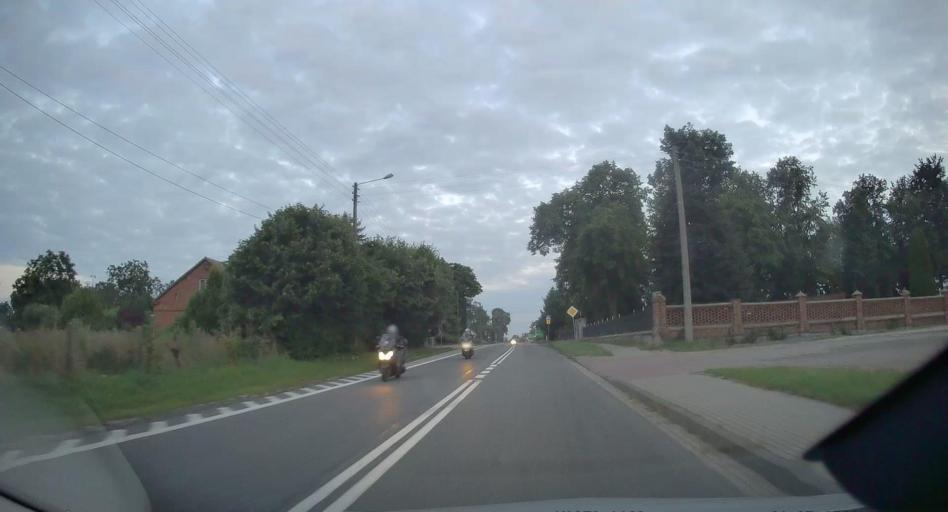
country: PL
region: Opole Voivodeship
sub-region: Powiat oleski
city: Dalachow
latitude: 51.0425
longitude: 18.5969
